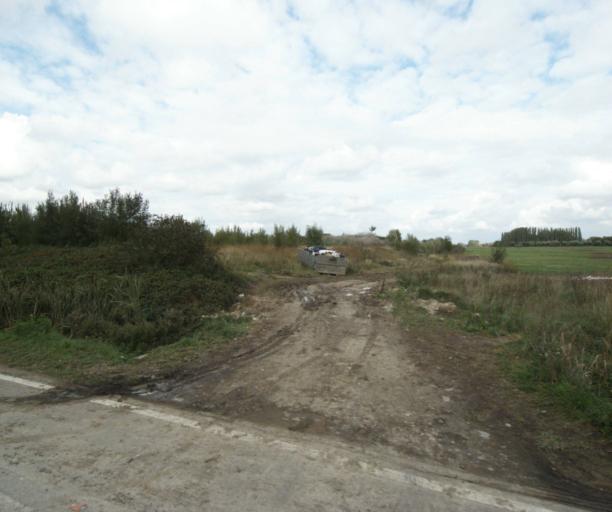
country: FR
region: Nord-Pas-de-Calais
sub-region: Departement du Nord
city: Premesques
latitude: 50.6563
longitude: 2.9328
